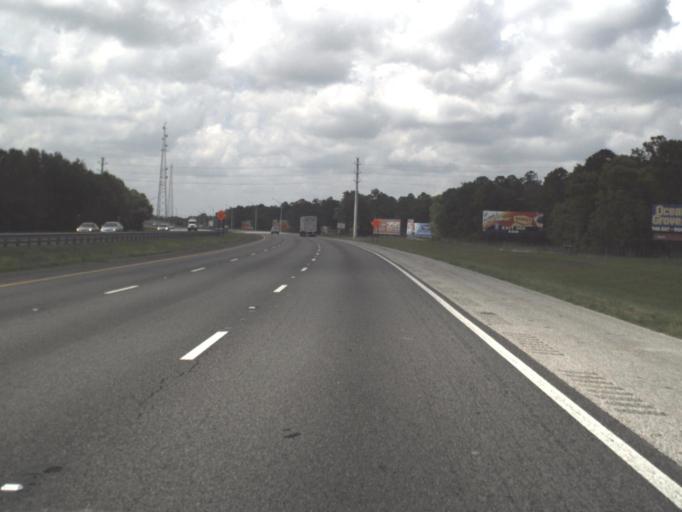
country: US
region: Florida
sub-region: Flagler County
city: Palm Coast
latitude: 29.6569
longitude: -81.2794
